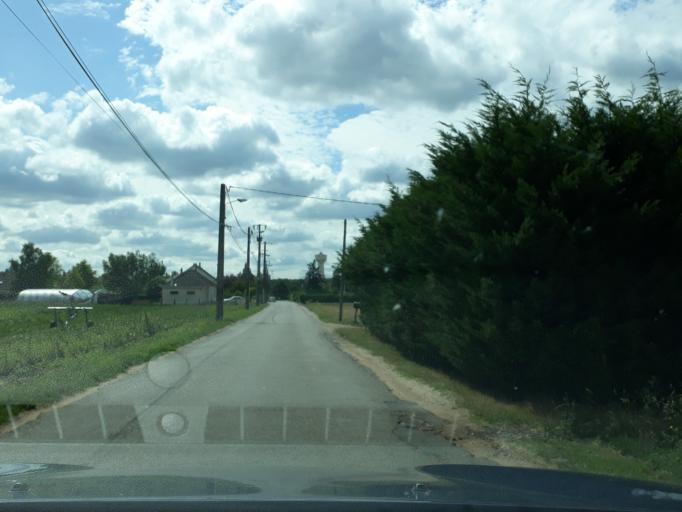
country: FR
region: Centre
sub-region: Departement du Loiret
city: Saint-Cyr-en-Val
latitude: 47.8383
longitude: 1.9690
